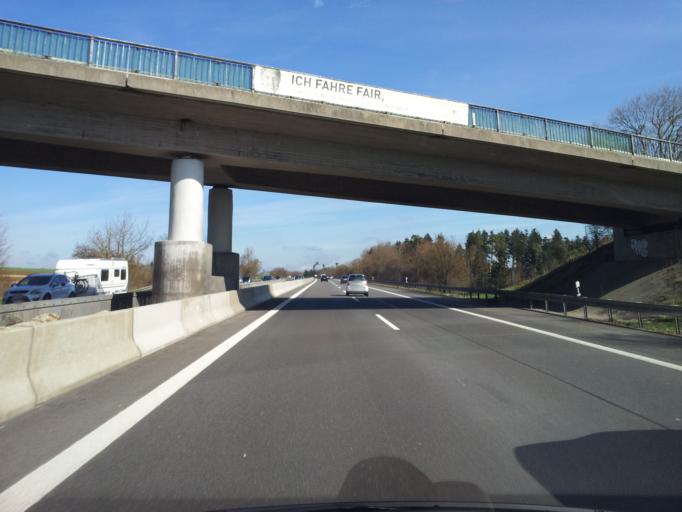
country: DE
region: Baden-Wuerttemberg
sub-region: Freiburg Region
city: Zimmern ob Rottweil
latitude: 48.1480
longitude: 8.5719
